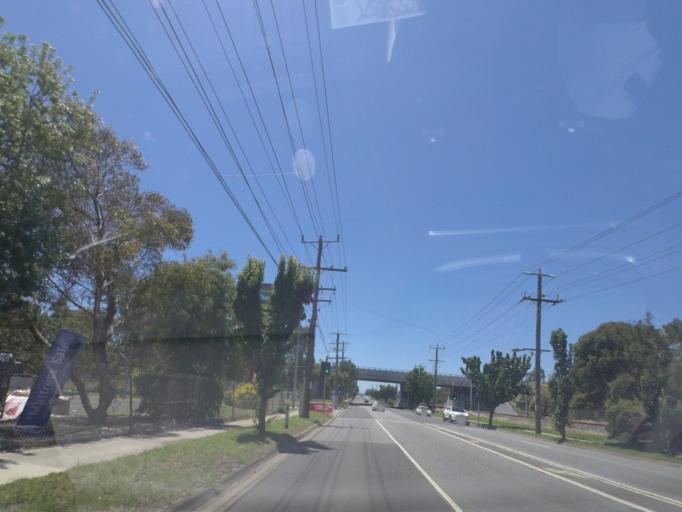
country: AU
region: Victoria
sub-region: Whittlesea
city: Thomastown
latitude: -37.6870
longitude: 145.0127
